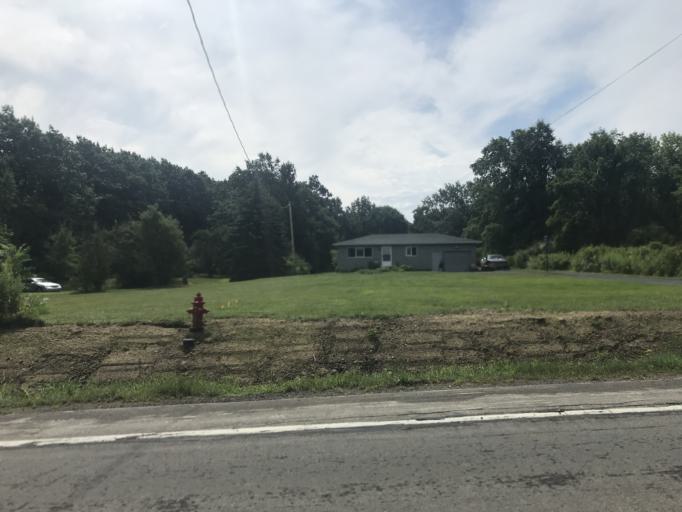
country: US
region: New York
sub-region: Chautauqua County
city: Silver Creek
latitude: 42.5447
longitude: -79.1922
